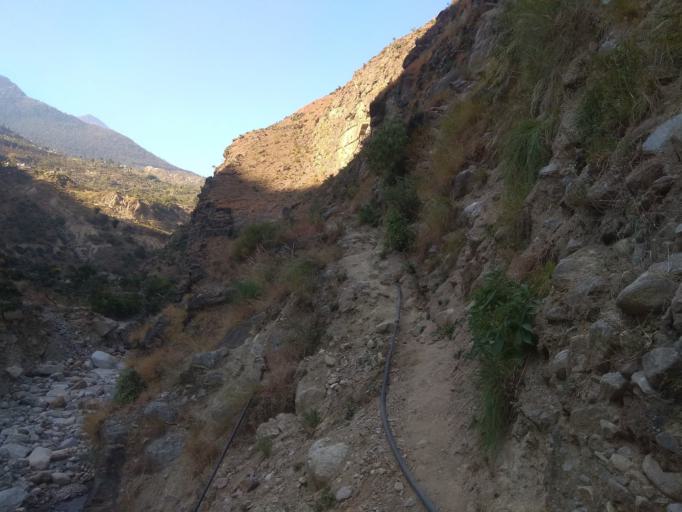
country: NP
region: Far Western
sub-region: Seti Zone
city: Achham
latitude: 29.2268
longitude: 81.6243
